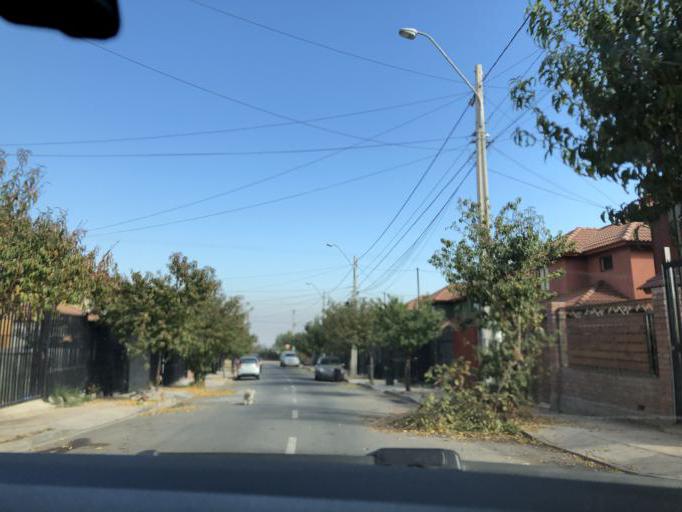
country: CL
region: Santiago Metropolitan
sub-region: Provincia de Cordillera
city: Puente Alto
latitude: -33.5775
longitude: -70.5420
